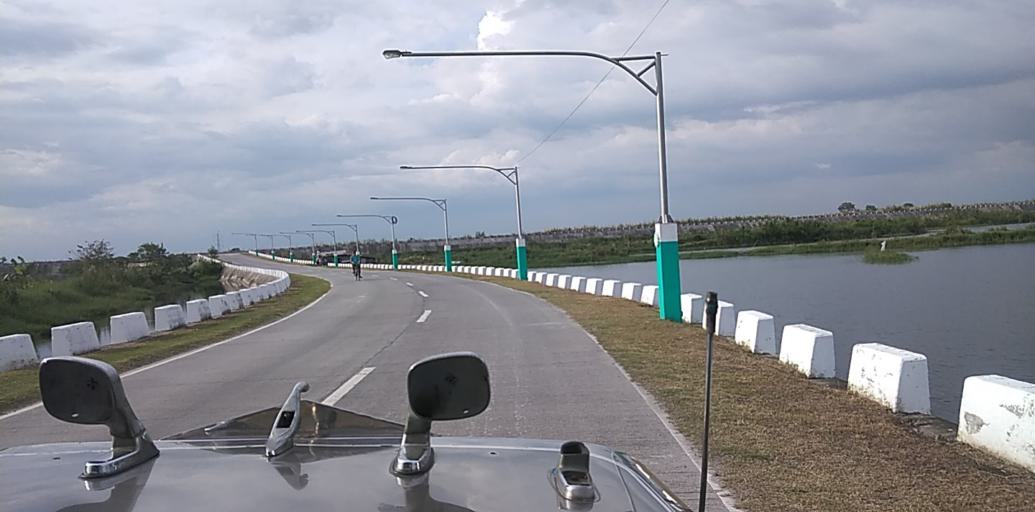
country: PH
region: Central Luzon
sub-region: Province of Pampanga
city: Minalin
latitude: 14.9750
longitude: 120.6825
